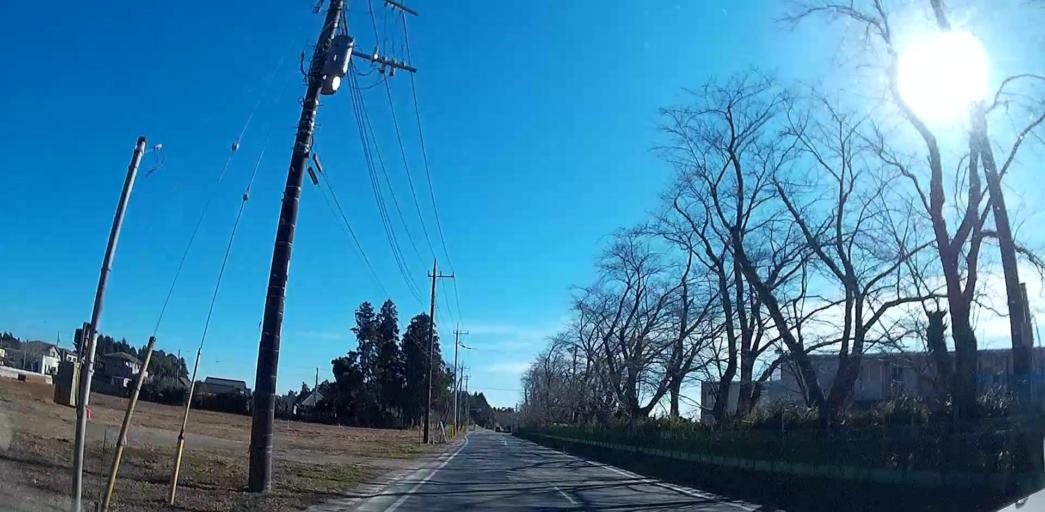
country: JP
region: Chiba
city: Narita
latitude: 35.7925
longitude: 140.3950
